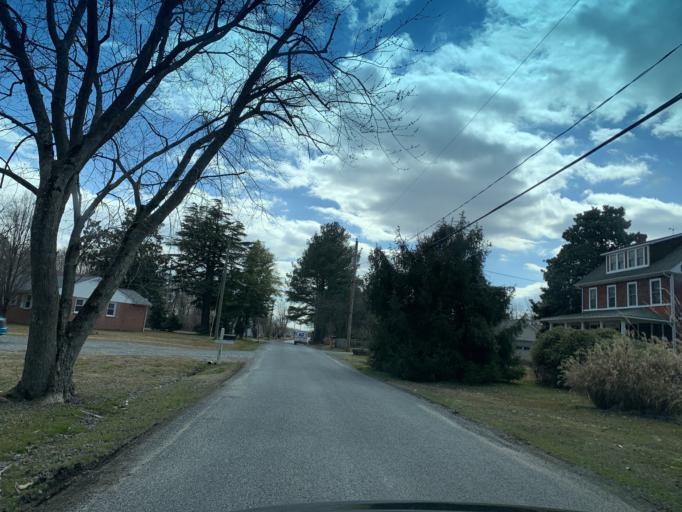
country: US
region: Maryland
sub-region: Queen Anne's County
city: Stevensville
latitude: 39.0330
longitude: -76.3111
